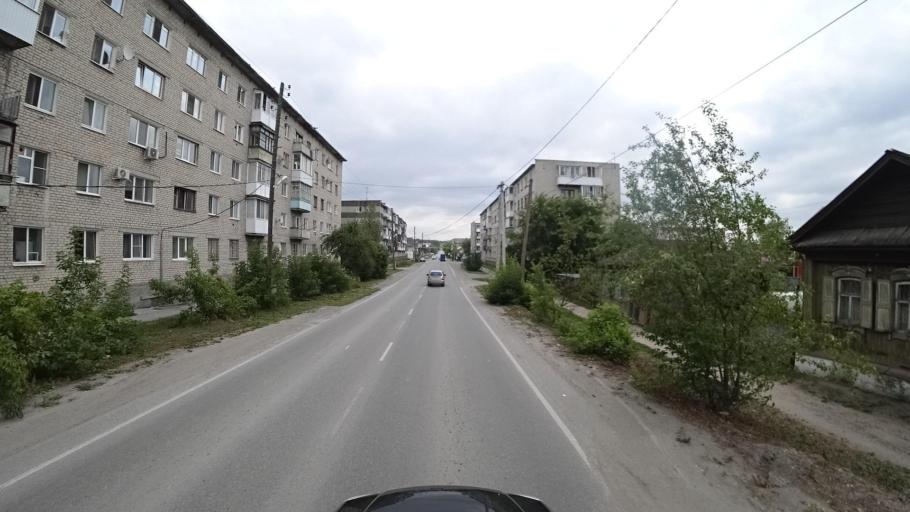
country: RU
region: Sverdlovsk
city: Kamyshlov
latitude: 56.8396
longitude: 62.7134
